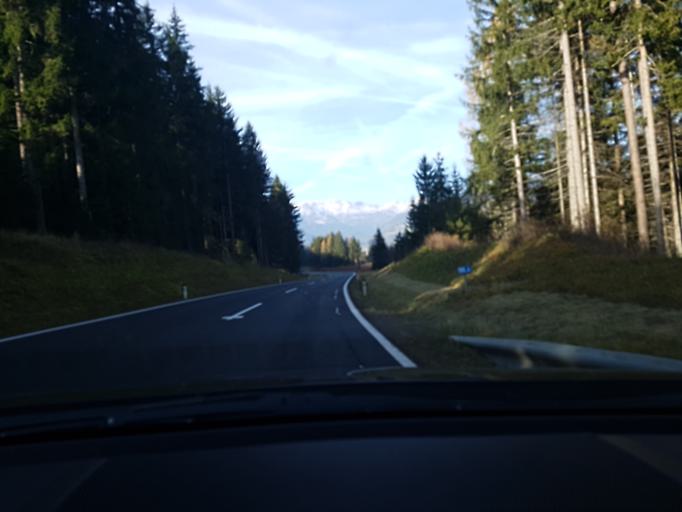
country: AT
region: Salzburg
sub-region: Politischer Bezirk Tamsweg
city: Sankt Andra im Lungau
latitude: 47.1396
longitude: 13.7704
